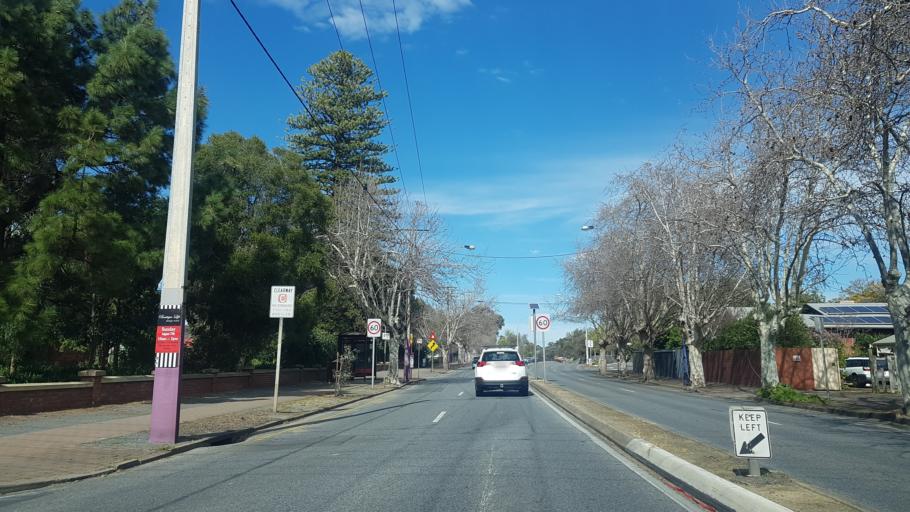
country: AU
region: South Australia
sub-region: Unley
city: Millswood
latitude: -34.9557
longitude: 138.5900
